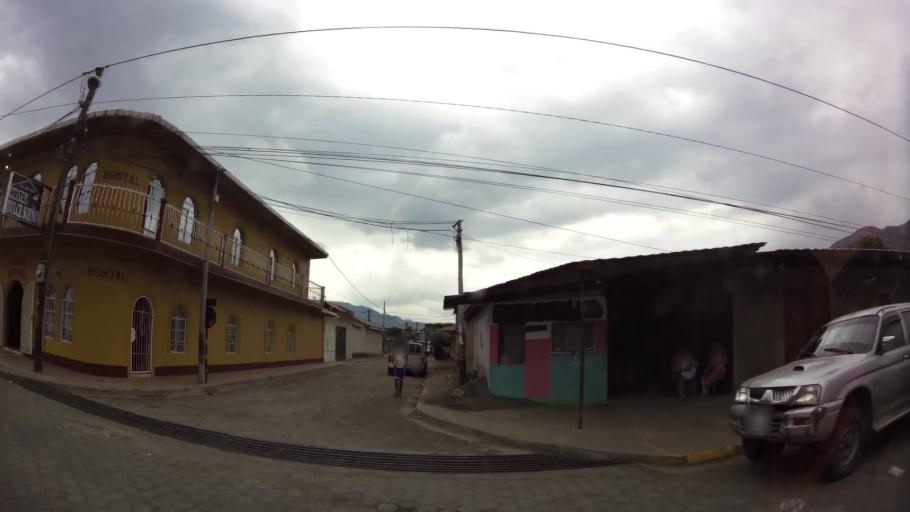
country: NI
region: Jinotega
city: Jinotega
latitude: 13.0977
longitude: -85.9995
